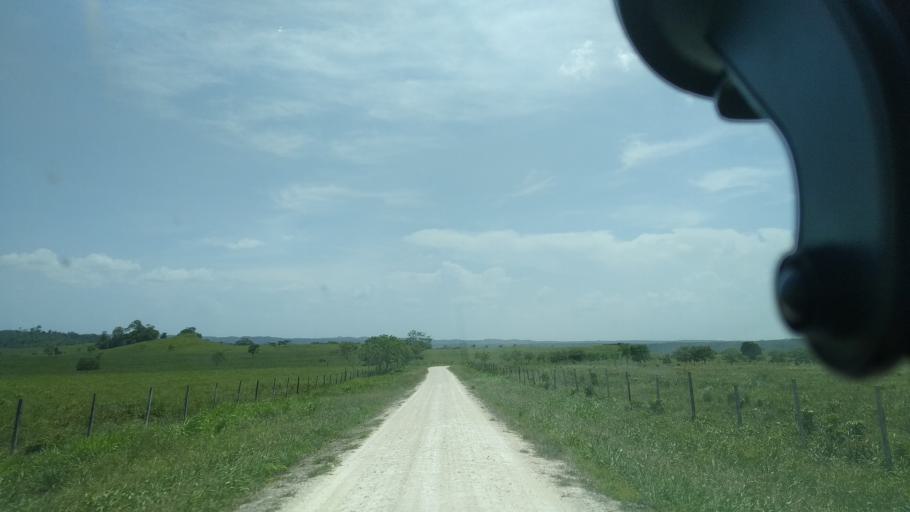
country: BZ
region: Cayo
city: San Ignacio
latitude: 17.2915
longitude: -89.0658
